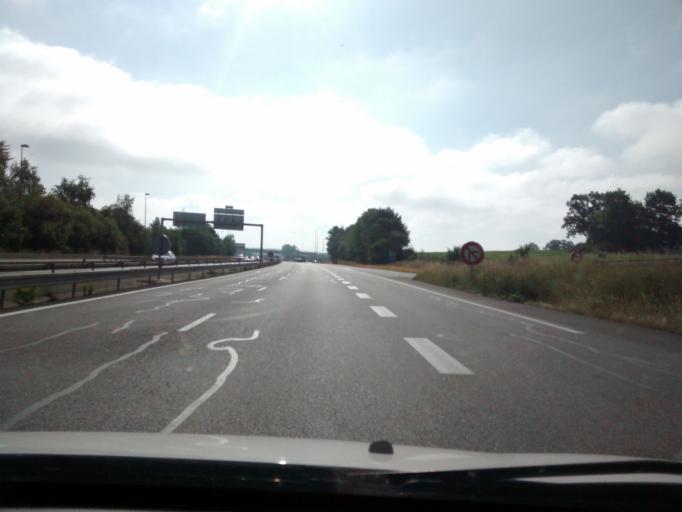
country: FR
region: Pays de la Loire
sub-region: Departement de la Mayenne
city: Saint-Pierre-la-Cour
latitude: 48.0827
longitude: -1.0351
